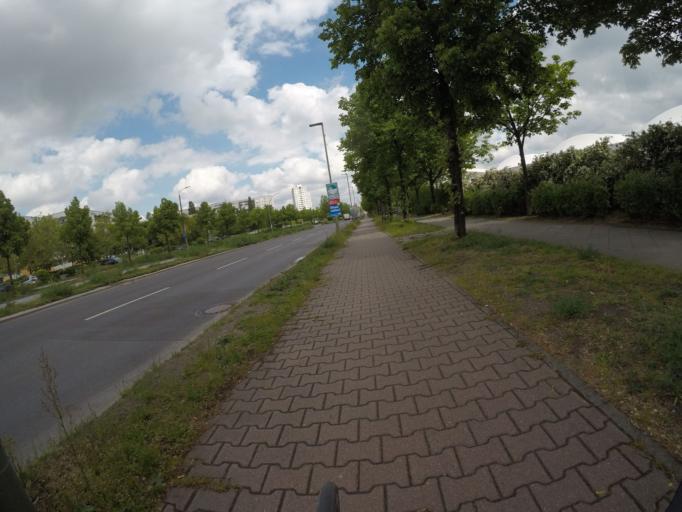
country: DE
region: Berlin
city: Marzahn
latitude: 52.5352
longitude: 13.5670
